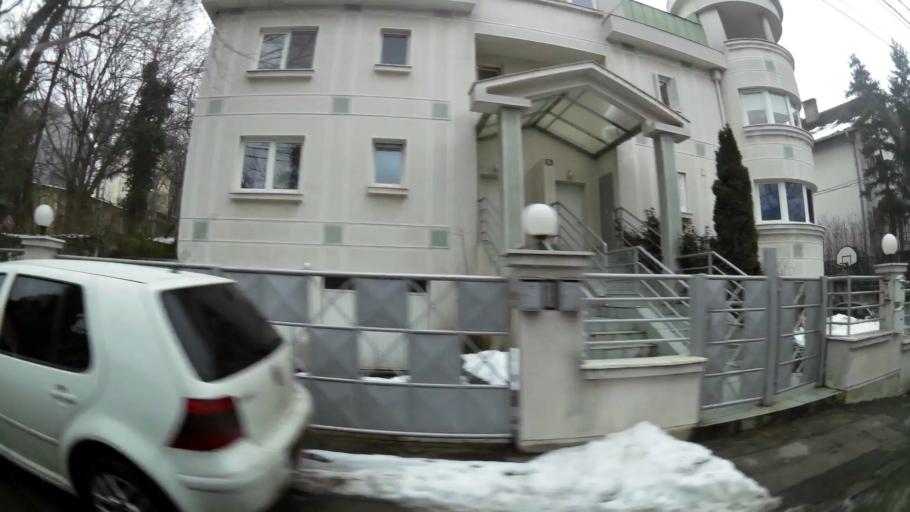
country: RS
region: Central Serbia
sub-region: Belgrade
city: Cukarica
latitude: 44.7900
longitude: 20.4327
